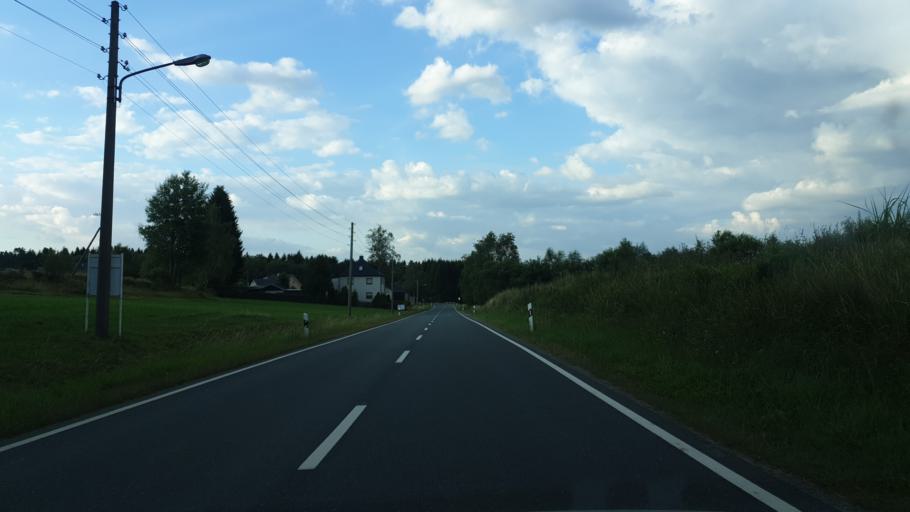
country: DE
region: Saxony
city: Hammerbrucke
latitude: 50.4377
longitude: 12.4159
